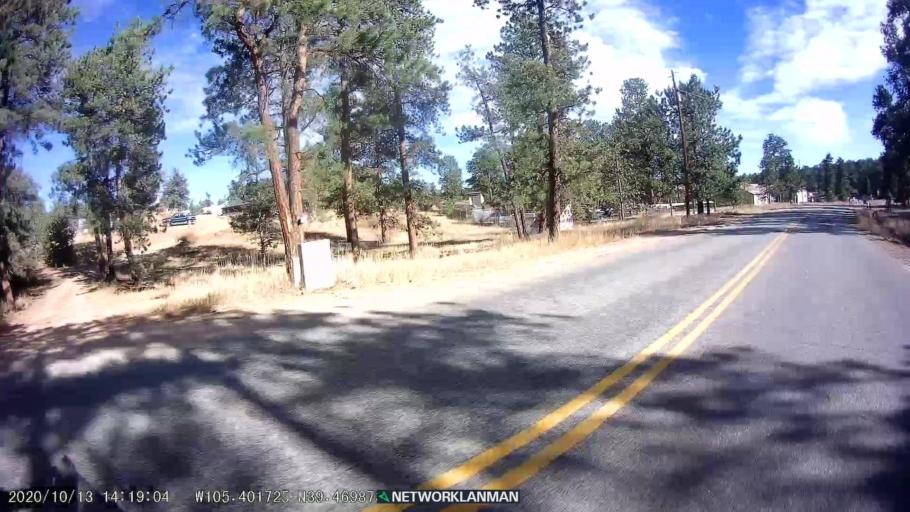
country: US
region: Colorado
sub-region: Jefferson County
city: Evergreen
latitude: 39.4697
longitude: -105.4016
